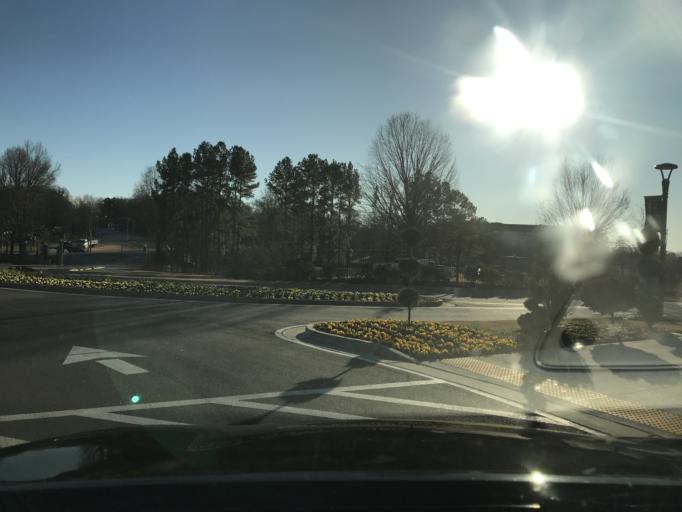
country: US
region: Georgia
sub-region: Fulton County
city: East Point
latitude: 33.7030
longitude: -84.4302
